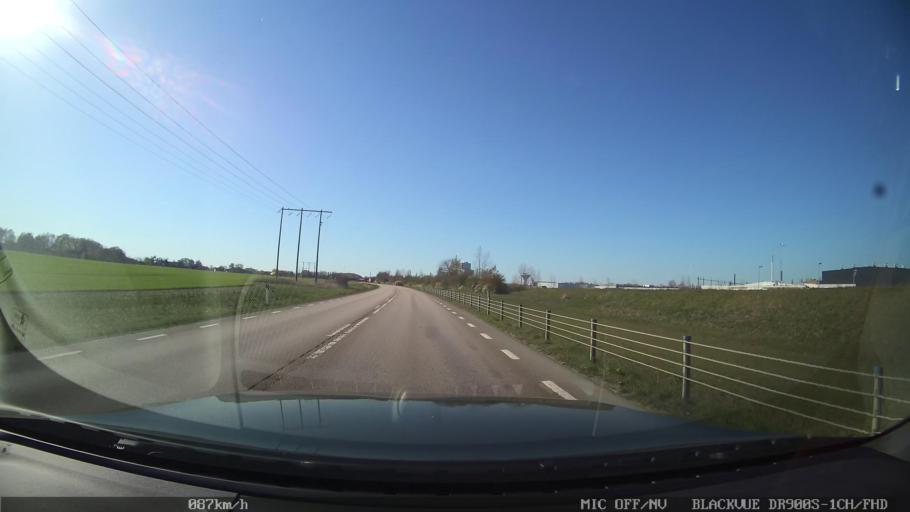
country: SE
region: Skane
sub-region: Bjuvs Kommun
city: Bjuv
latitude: 56.0691
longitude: 12.9396
